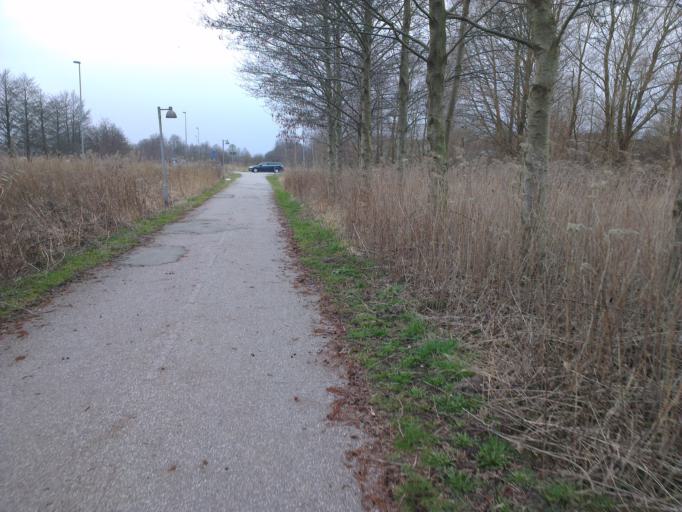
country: DK
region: Capital Region
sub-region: Frederikssund Kommune
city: Frederikssund
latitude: 55.8576
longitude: 12.0808
